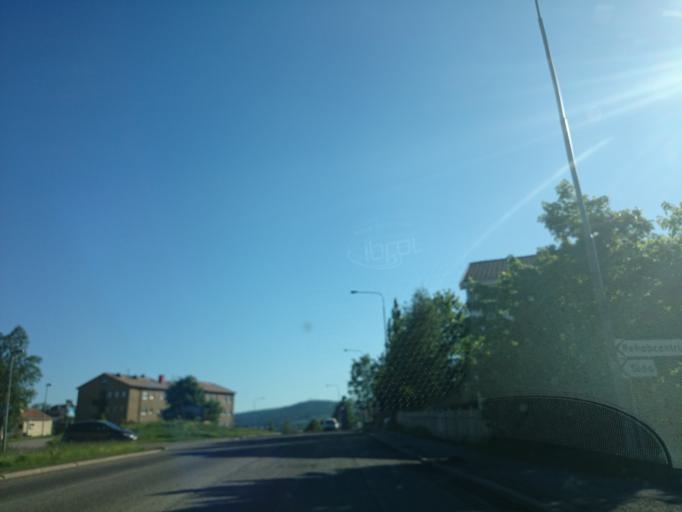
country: SE
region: Vaesternorrland
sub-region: Haernoesands Kommun
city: Haernoesand
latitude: 62.6270
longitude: 17.9295
